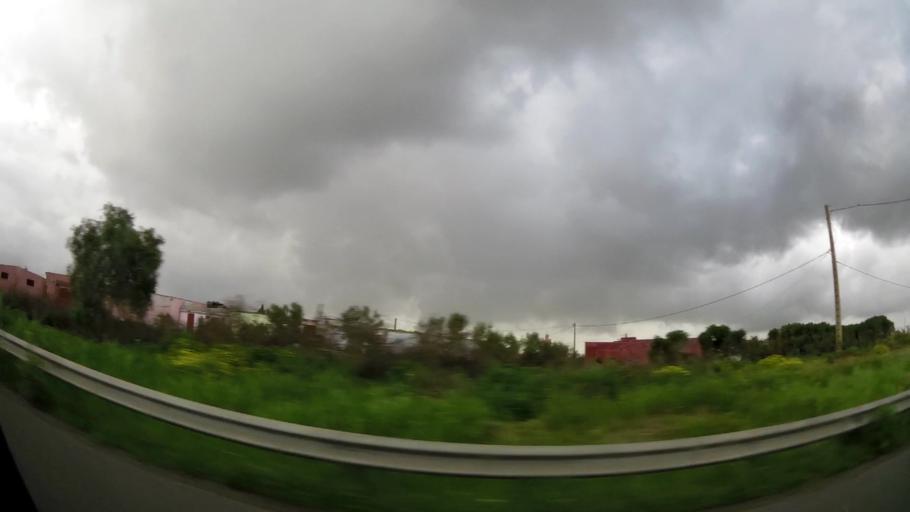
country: MA
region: Grand Casablanca
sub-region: Mediouna
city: Tit Mellil
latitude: 33.5725
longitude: -7.4573
